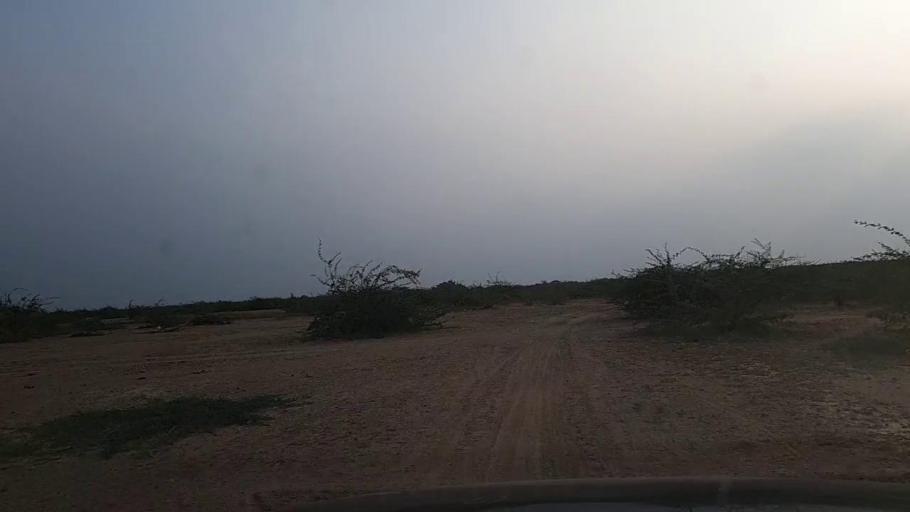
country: PK
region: Sindh
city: Gharo
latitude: 24.7743
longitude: 67.7068
